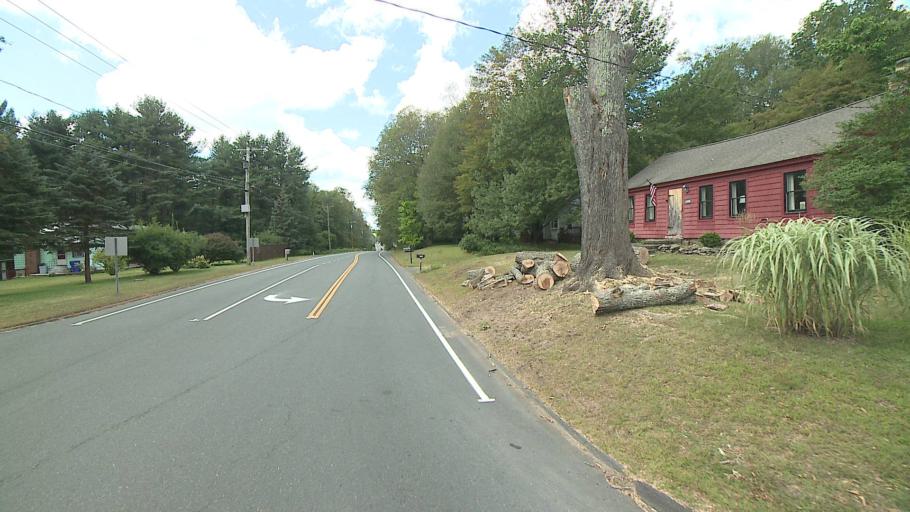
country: US
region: Connecticut
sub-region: Tolland County
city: Coventry Lake
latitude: 41.7987
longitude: -72.3617
